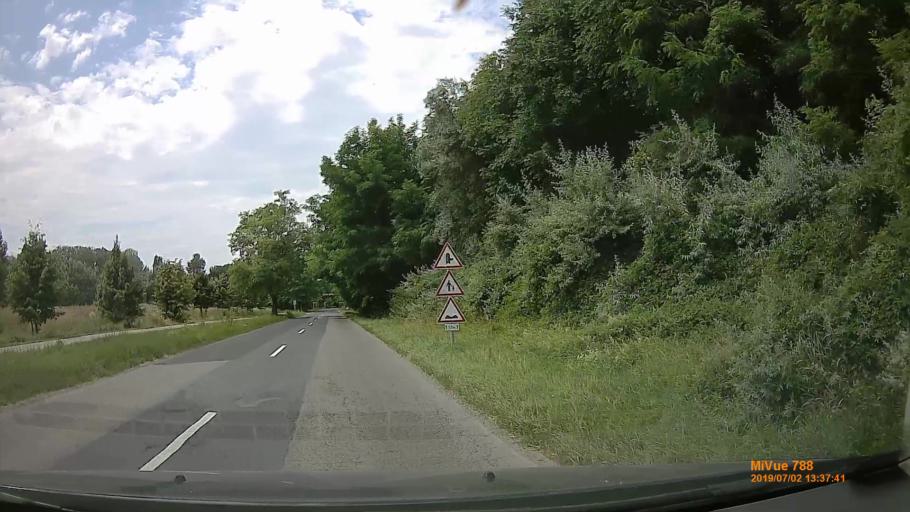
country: HU
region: Gyor-Moson-Sopron
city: Mosonmagyarovar
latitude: 47.8560
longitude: 17.2946
